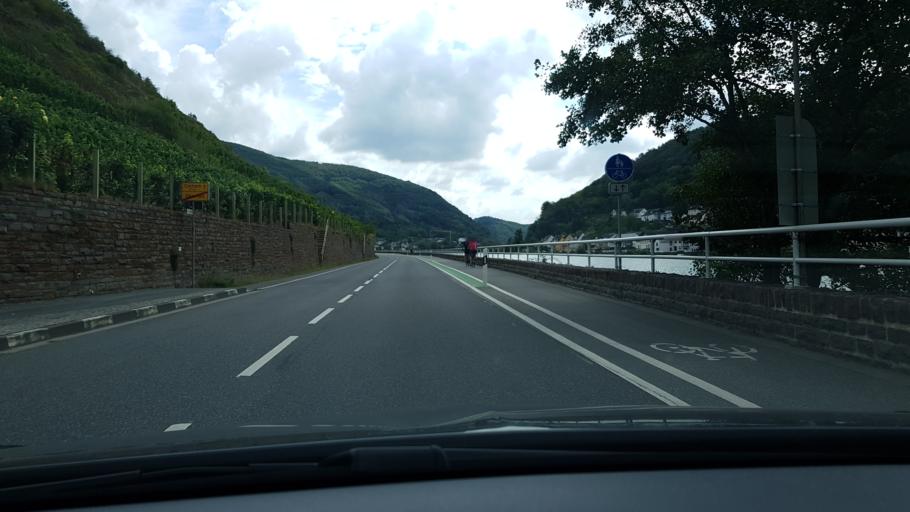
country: DE
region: Rheinland-Pfalz
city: Oberfell
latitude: 50.2553
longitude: 7.4428
